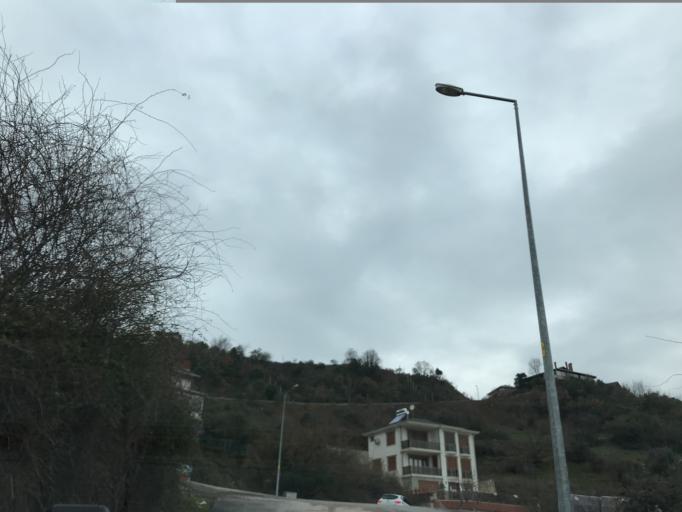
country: TR
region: Yalova
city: Termal
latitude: 40.5970
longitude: 29.1706
